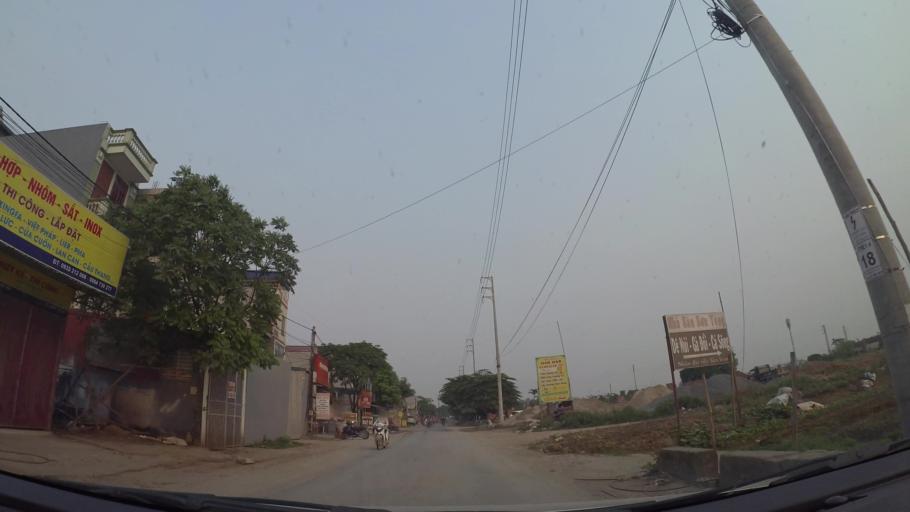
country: VN
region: Ha Noi
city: Cau Dien
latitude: 21.0047
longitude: 105.7207
